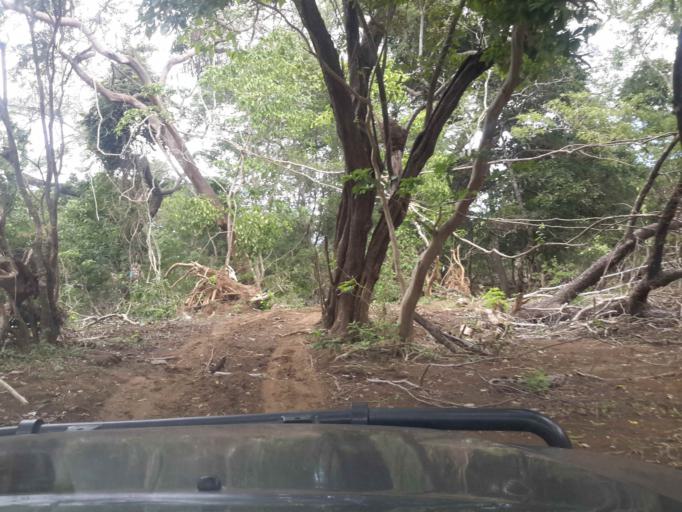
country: NI
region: Carazo
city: Santa Teresa
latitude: 11.6897
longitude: -86.2948
